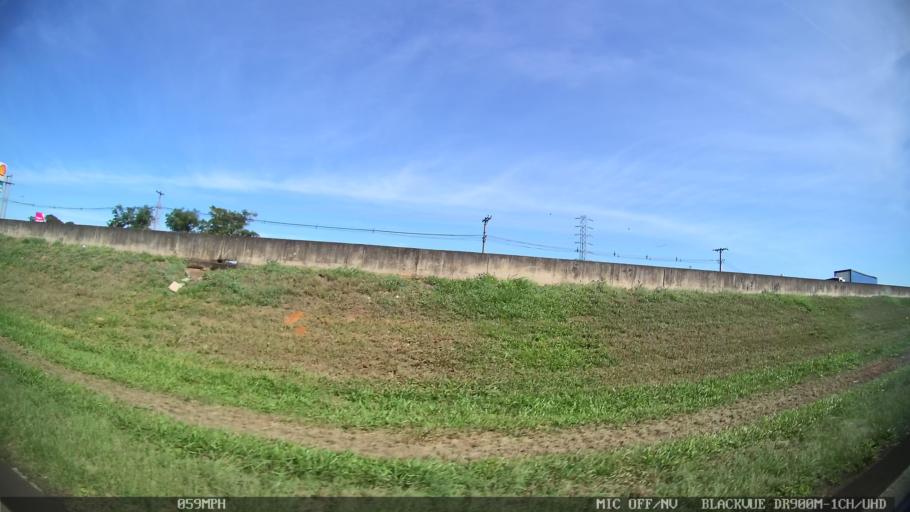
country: BR
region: Sao Paulo
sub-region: Pirassununga
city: Pirassununga
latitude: -21.9997
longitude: -47.4452
